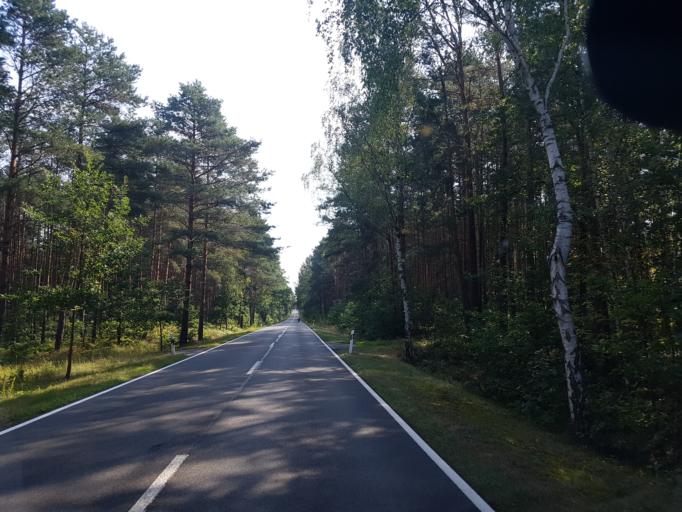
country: DE
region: Brandenburg
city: Lauchhammer
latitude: 51.5299
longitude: 13.6941
